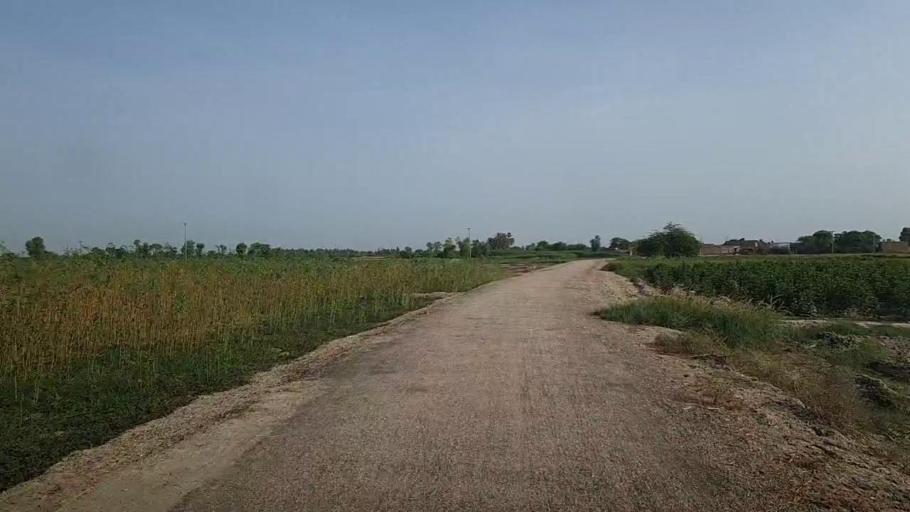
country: PK
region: Sindh
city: Pad Idan
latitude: 26.7524
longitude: 68.2575
